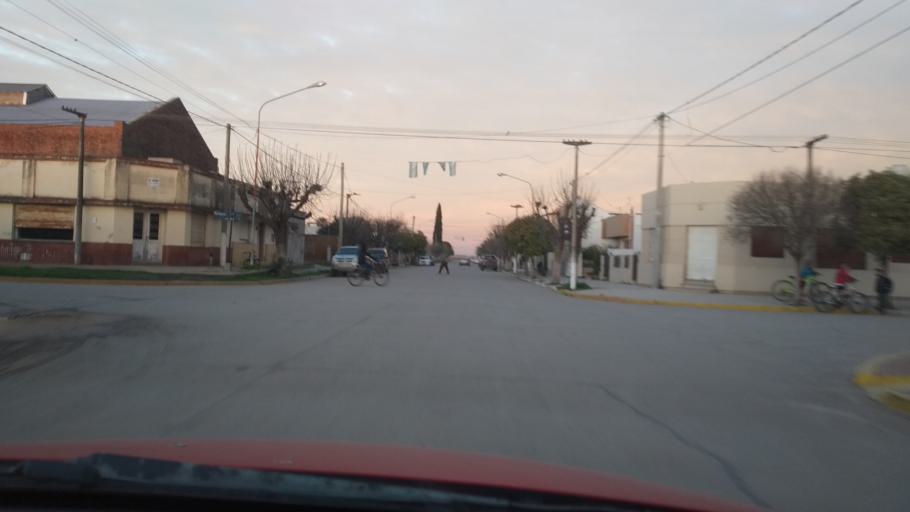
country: AR
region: Cordoba
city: Leones
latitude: -32.6304
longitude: -62.4786
